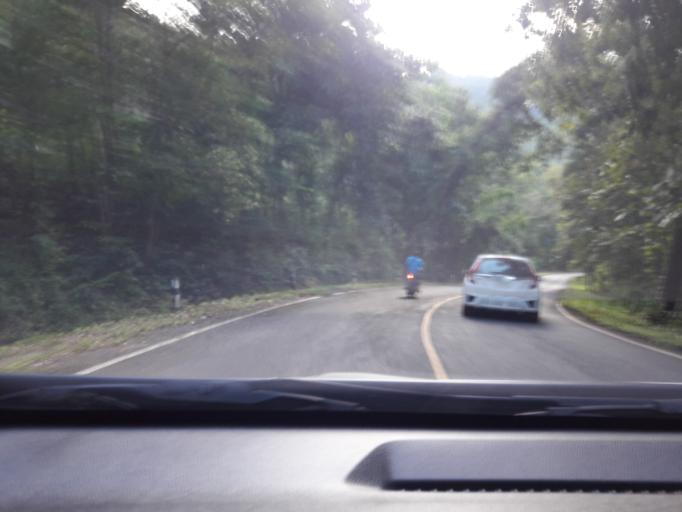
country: TH
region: Mae Hong Son
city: Sop Pong
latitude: 19.5629
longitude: 98.1955
